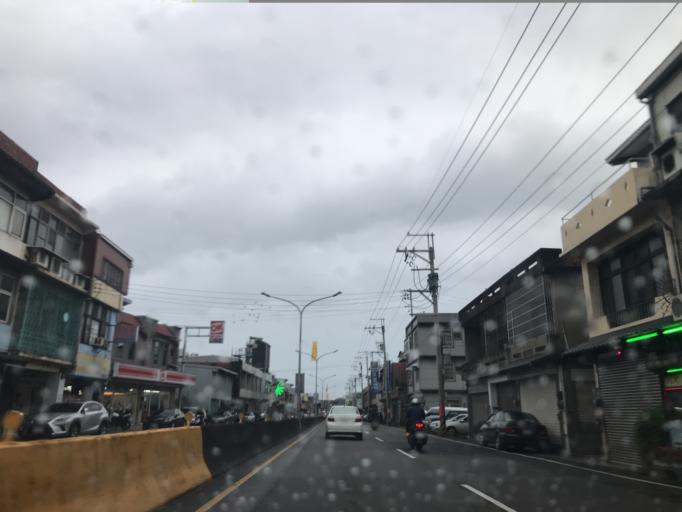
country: TW
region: Taiwan
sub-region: Hsinchu
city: Zhubei
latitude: 24.8263
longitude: 121.0536
